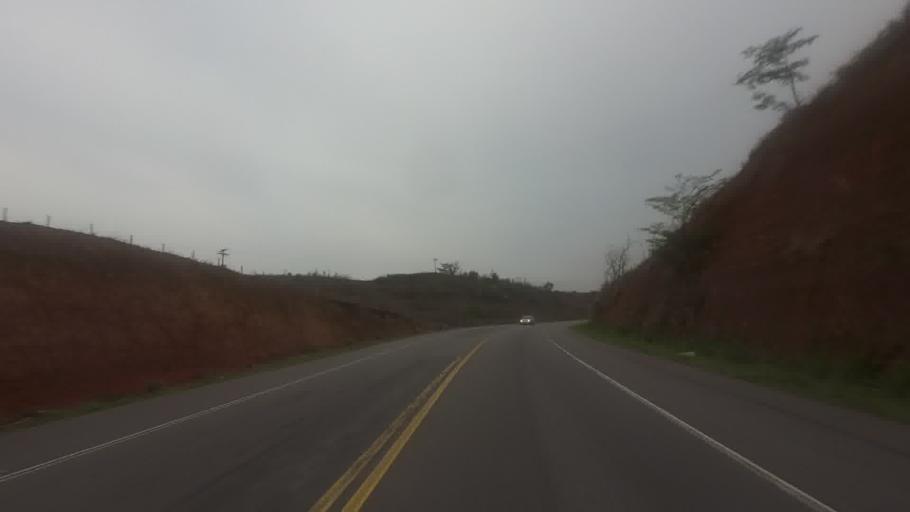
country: BR
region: Minas Gerais
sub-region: Recreio
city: Recreio
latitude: -21.6775
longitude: -42.3929
